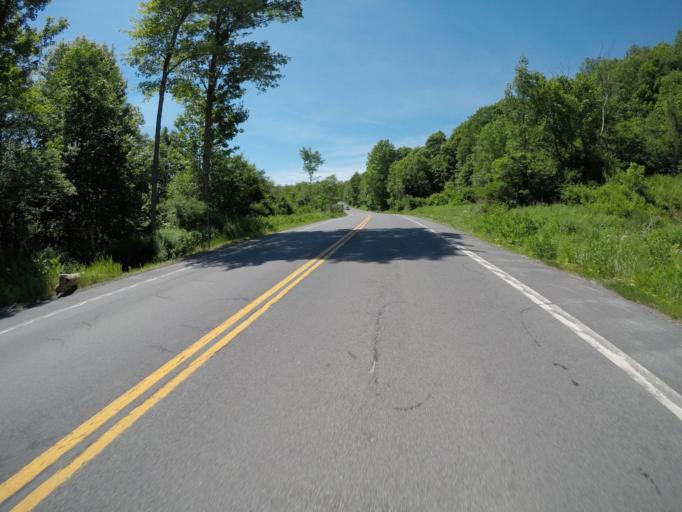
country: US
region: New York
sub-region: Delaware County
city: Delhi
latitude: 42.2331
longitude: -74.9706
